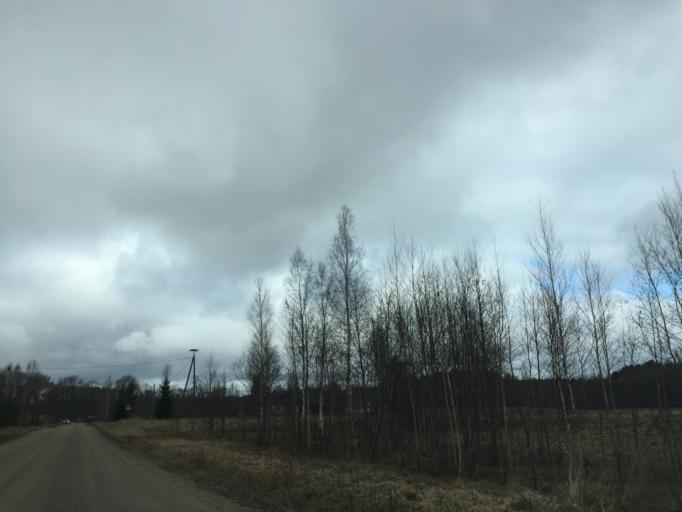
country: LV
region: Ilukste
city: Ilukste
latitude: 56.0658
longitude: 26.1489
